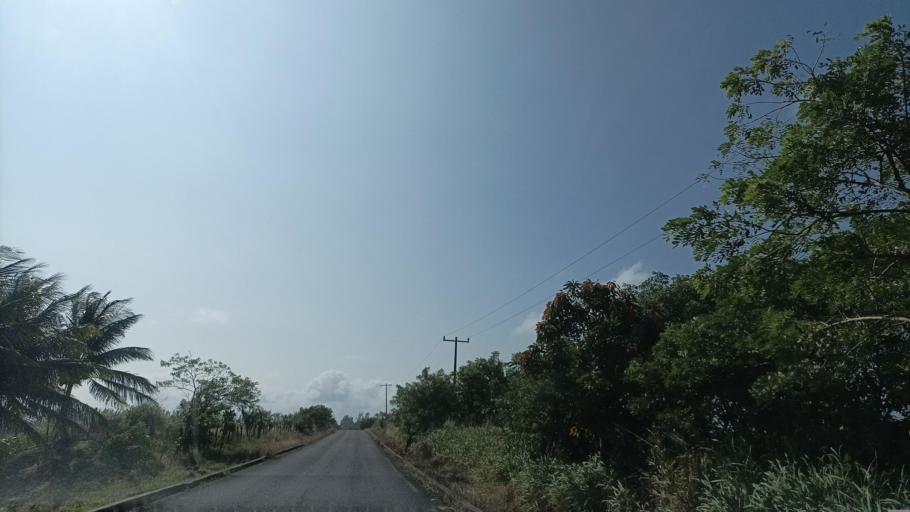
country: MX
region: Veracruz
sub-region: Pajapan
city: Pajapan
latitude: 18.2250
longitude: -94.6174
